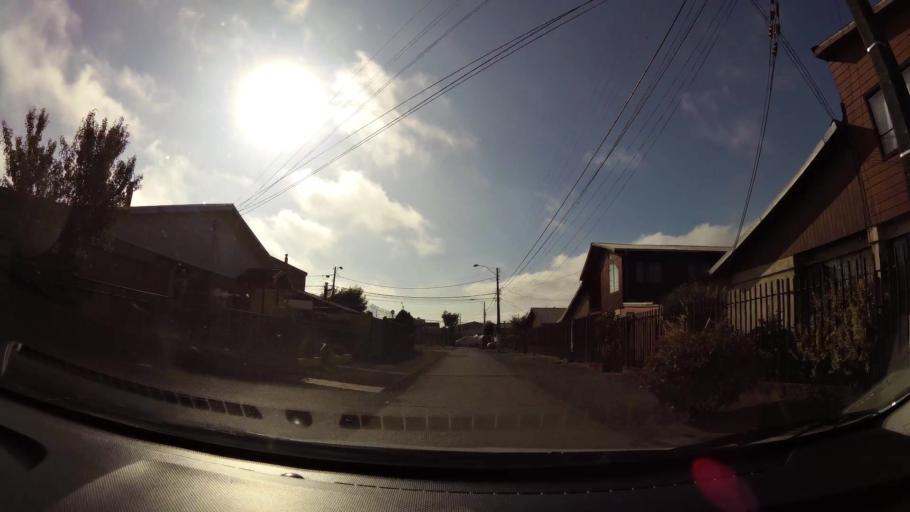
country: CL
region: Biobio
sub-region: Provincia de Concepcion
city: Concepcion
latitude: -36.7938
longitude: -73.1003
